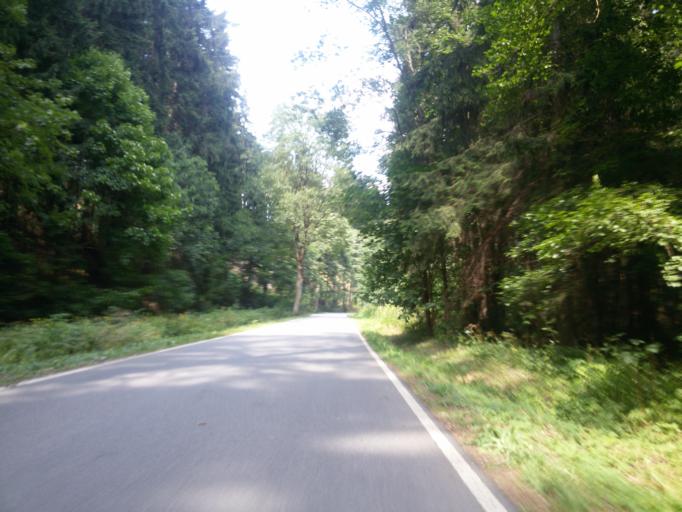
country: CZ
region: South Moravian
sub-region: Okres Brno-Venkov
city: Lomnice
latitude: 49.4564
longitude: 16.4370
